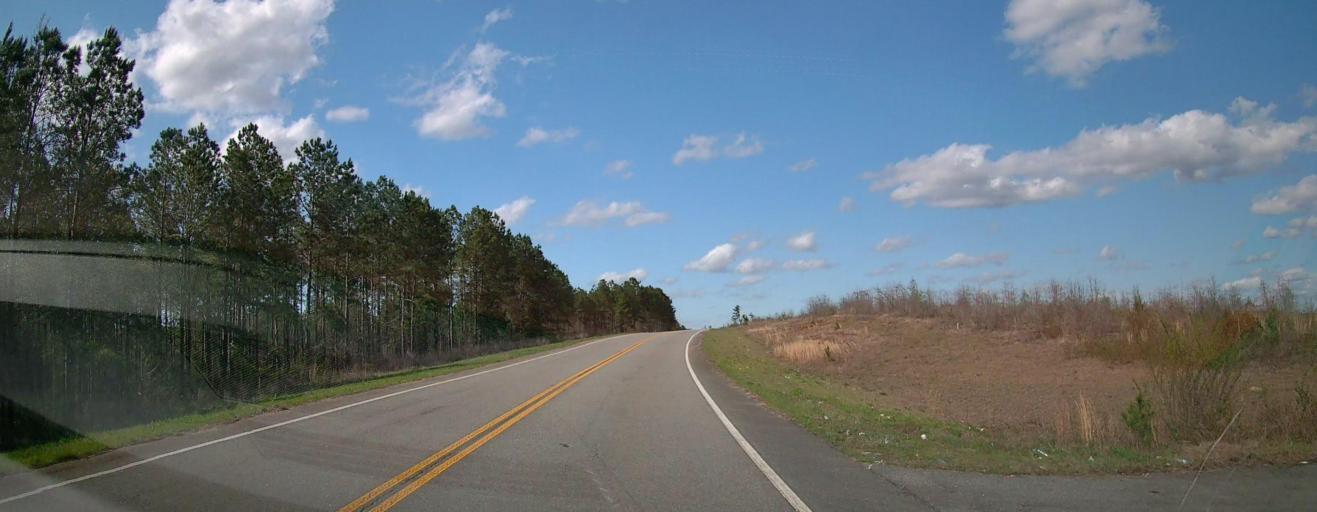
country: US
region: Georgia
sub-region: Wilkinson County
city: Gordon
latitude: 32.9425
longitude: -83.2895
